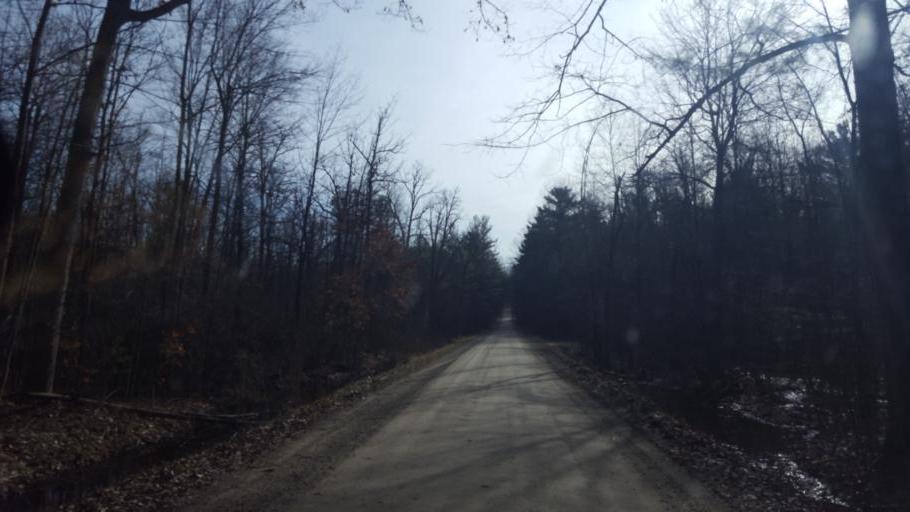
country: US
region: Michigan
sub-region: Montcalm County
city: Howard City
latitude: 43.5403
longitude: -85.5601
